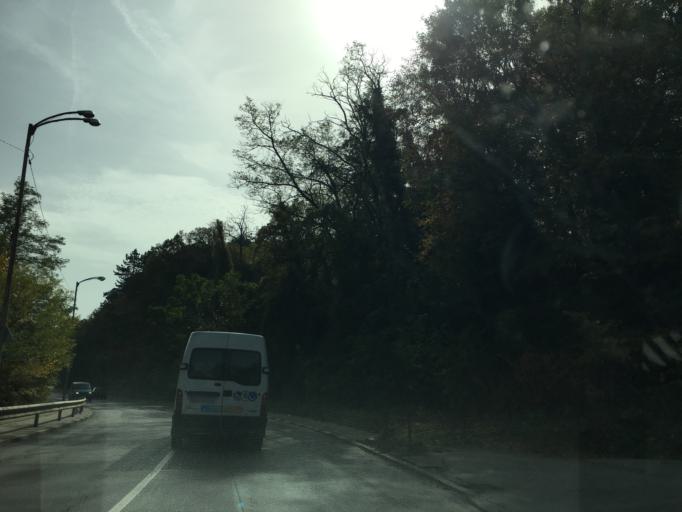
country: BG
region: Sofia-Capital
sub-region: Stolichna Obshtina
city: Sofia
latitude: 42.5941
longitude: 23.4156
